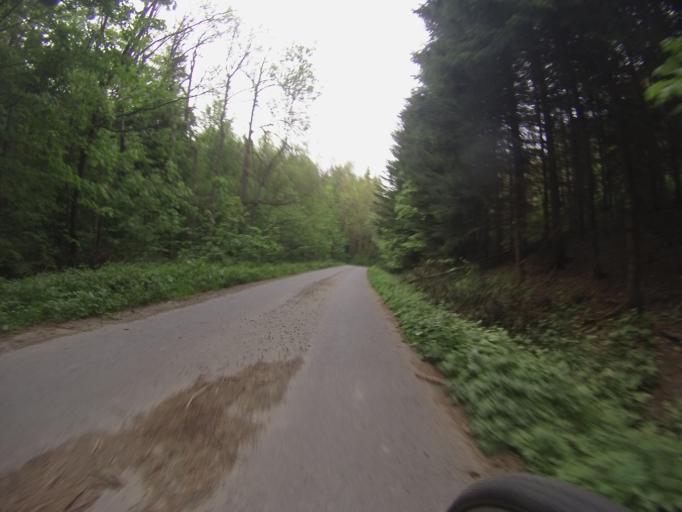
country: CZ
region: Olomoucky
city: Protivanov
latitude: 49.4687
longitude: 16.8795
